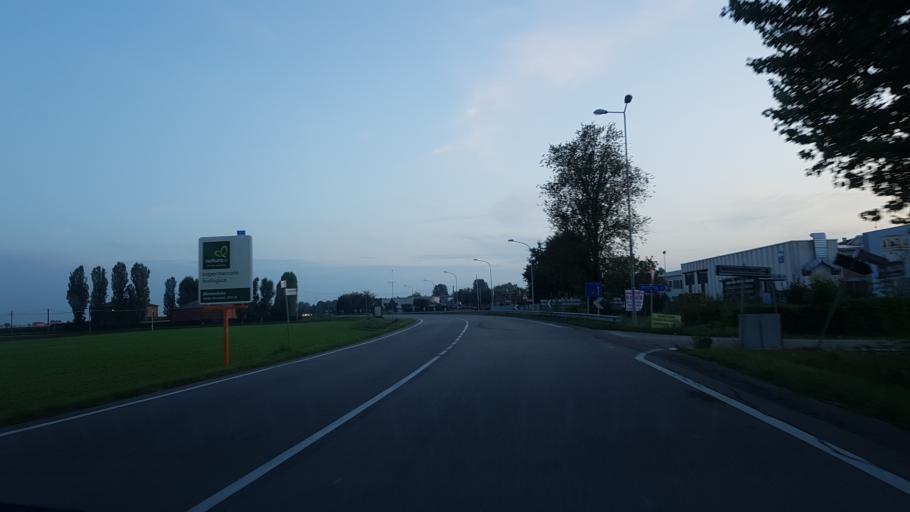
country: IT
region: Emilia-Romagna
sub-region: Provincia di Modena
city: San Prospero
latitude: 44.8105
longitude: 11.0306
